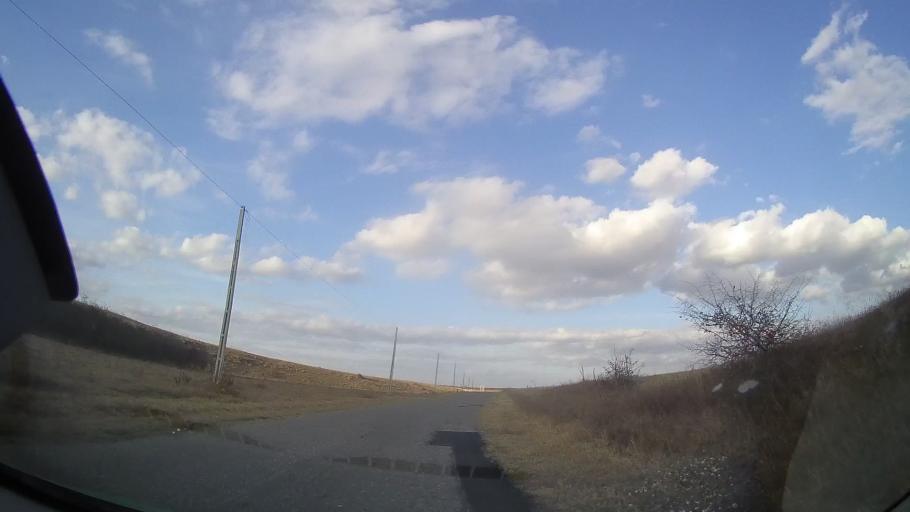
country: RO
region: Constanta
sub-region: Comuna Cerchezu
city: Cerchezu
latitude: 43.8376
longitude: 28.0974
